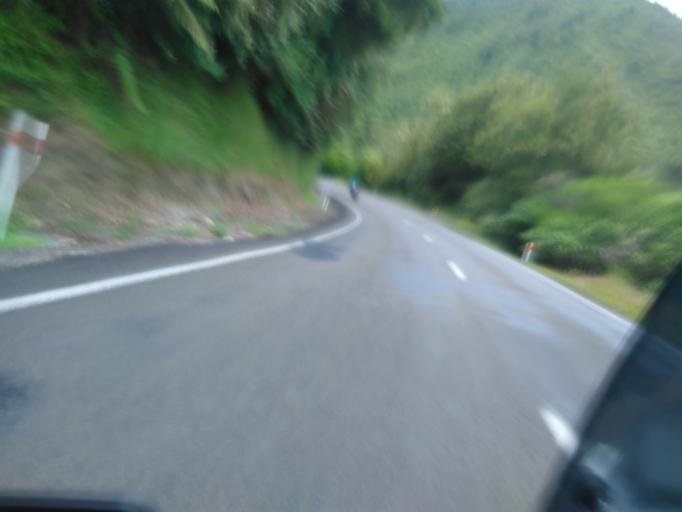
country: NZ
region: Bay of Plenty
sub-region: Opotiki District
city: Opotiki
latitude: -38.2365
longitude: 177.3093
